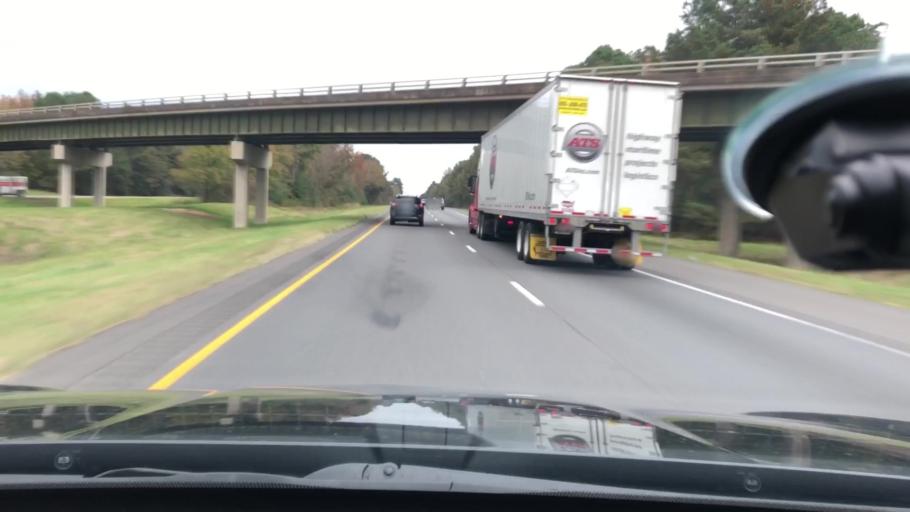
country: US
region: Arkansas
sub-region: Hempstead County
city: Hope
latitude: 33.7029
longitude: -93.5817
